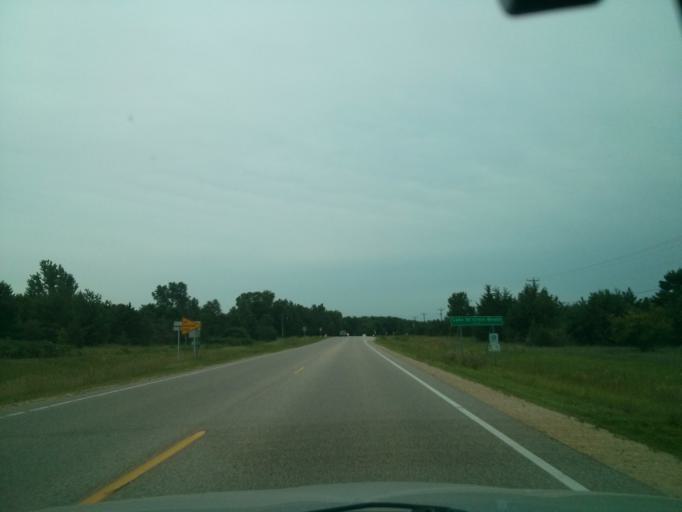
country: US
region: Minnesota
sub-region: Washington County
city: Lake Saint Croix Beach
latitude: 44.9314
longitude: -92.7711
